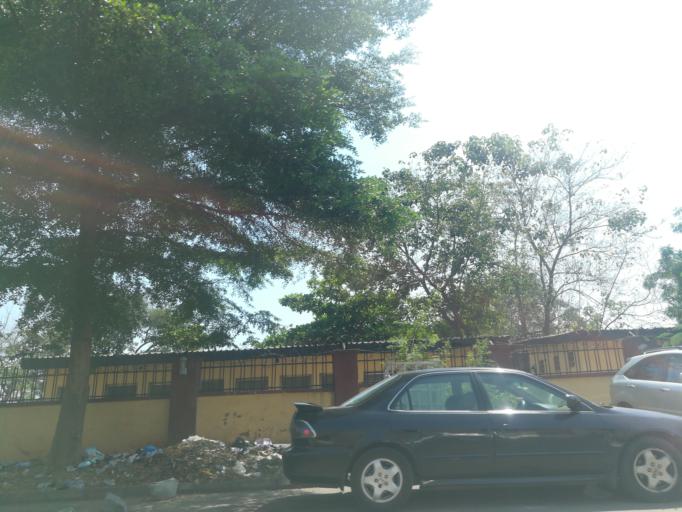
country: NG
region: Abuja Federal Capital Territory
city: Abuja
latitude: 9.0712
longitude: 7.4510
